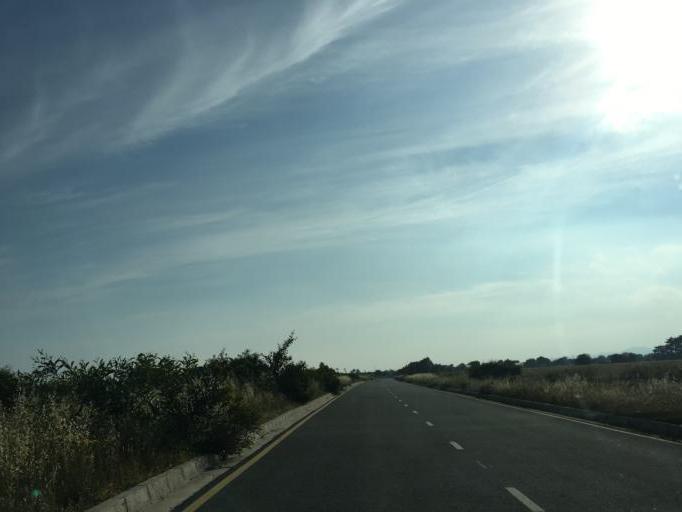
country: CY
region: Larnaka
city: Tersefanou
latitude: 34.8034
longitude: 33.5230
